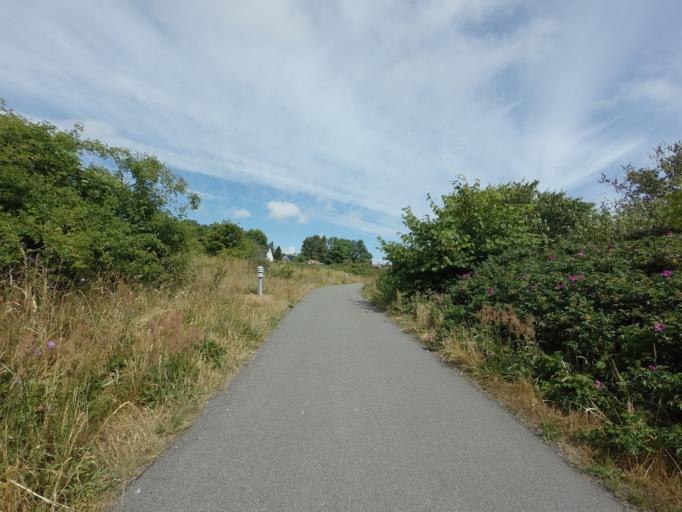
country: SE
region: Skane
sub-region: Simrishamns Kommun
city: Simrishamn
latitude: 55.5236
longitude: 14.3474
